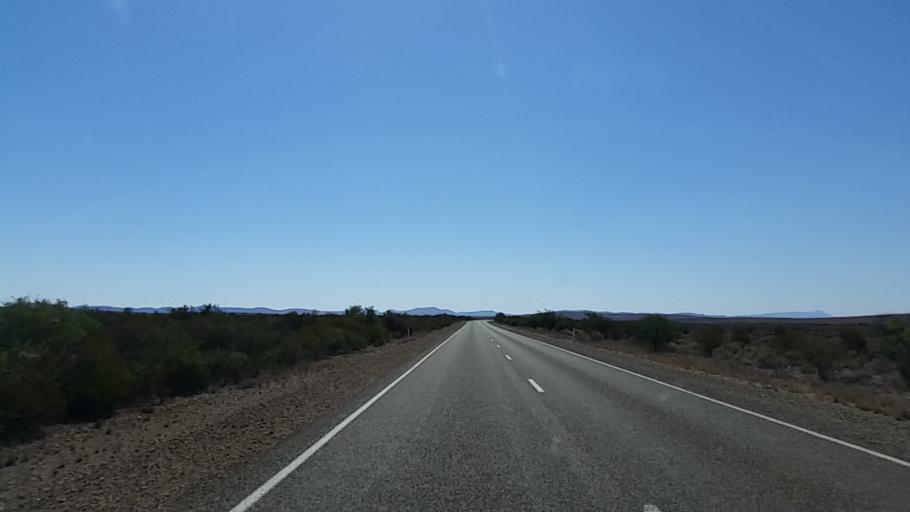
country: AU
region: South Australia
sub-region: Flinders Ranges
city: Quorn
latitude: -32.1250
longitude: 138.5090
